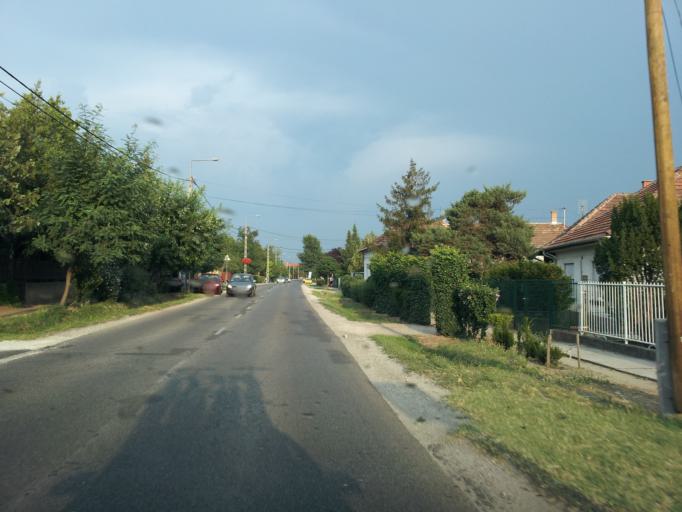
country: HU
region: Pest
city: Dunaharaszti
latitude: 47.3511
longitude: 19.1015
